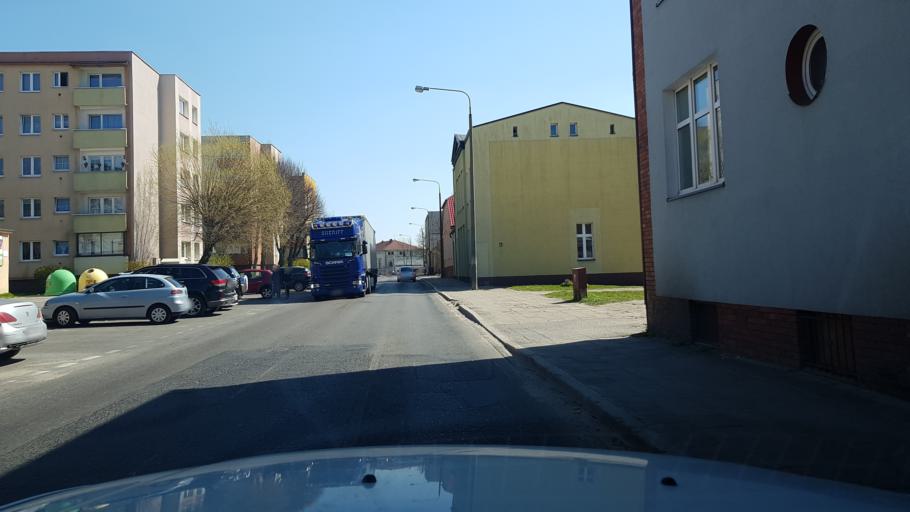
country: PL
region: West Pomeranian Voivodeship
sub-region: Powiat slawienski
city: Slawno
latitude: 54.3649
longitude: 16.6808
